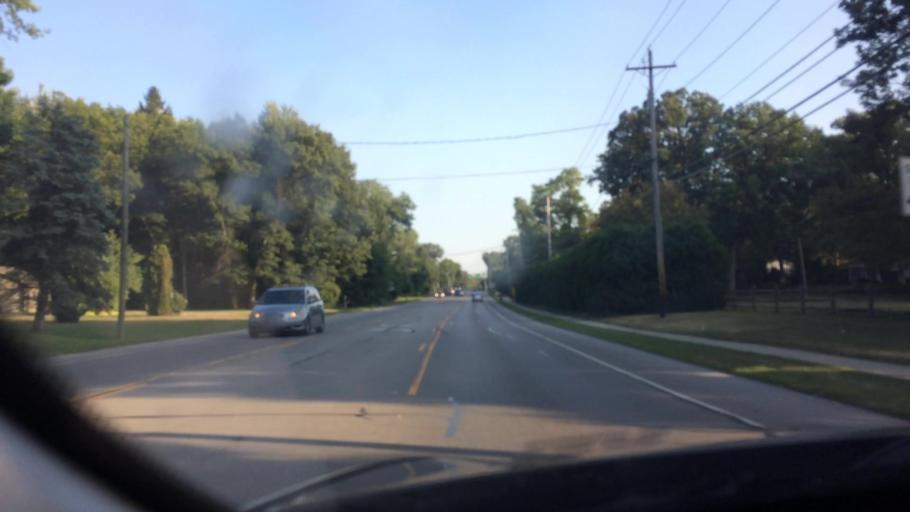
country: US
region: Ohio
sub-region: Lucas County
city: Holland
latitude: 41.6678
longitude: -83.7027
